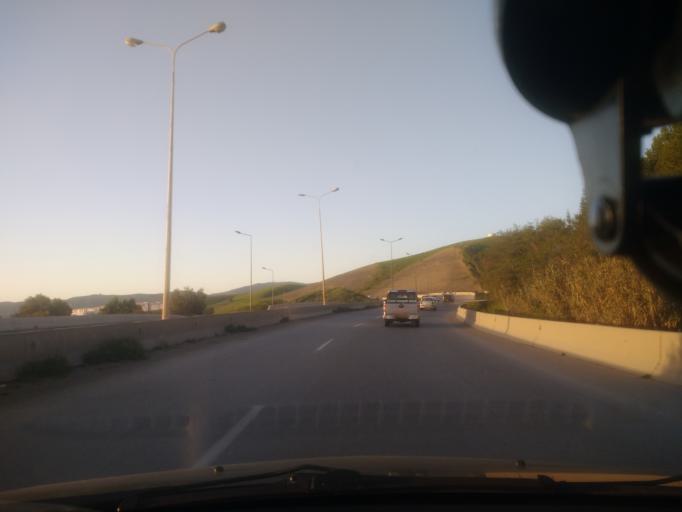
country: DZ
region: Tizi Ouzou
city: Tizi Ouzou
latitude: 36.7159
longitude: 4.0026
